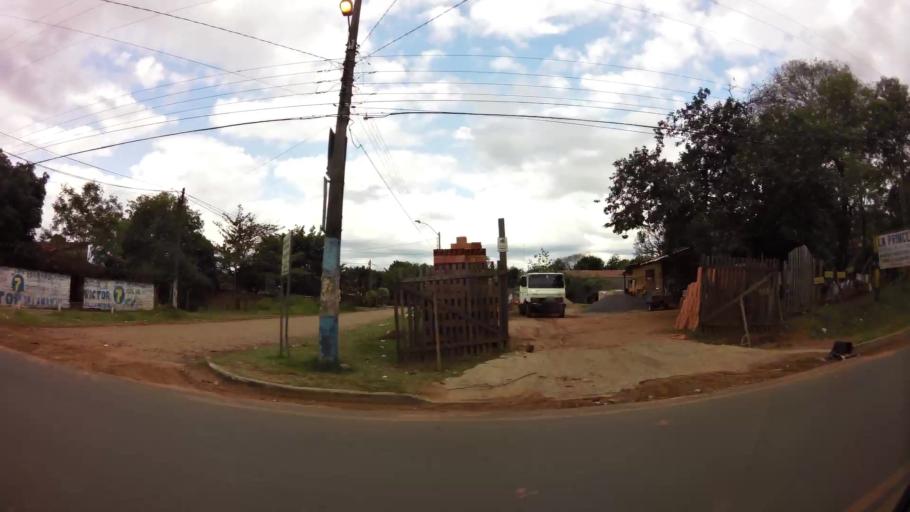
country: PY
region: Central
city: San Lorenzo
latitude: -25.2893
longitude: -57.4825
